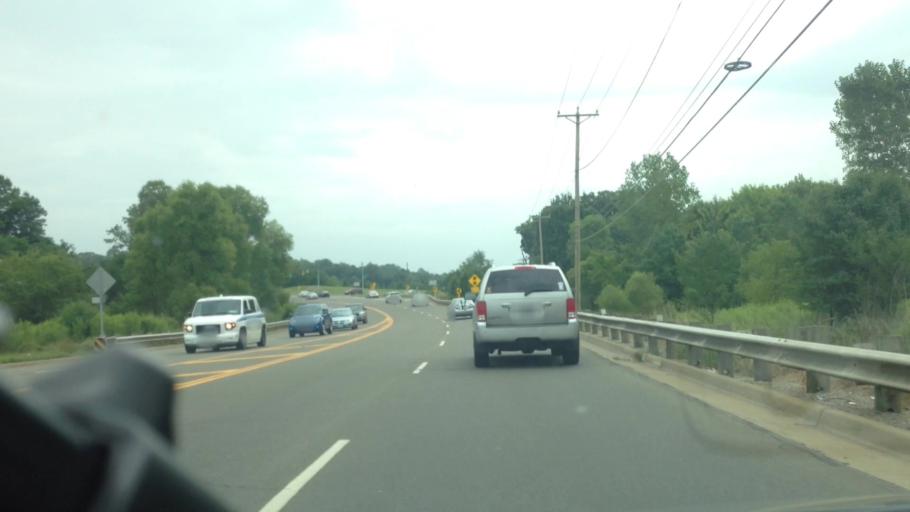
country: US
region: Ohio
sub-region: Stark County
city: Perry Heights
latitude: 40.8342
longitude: -81.4620
